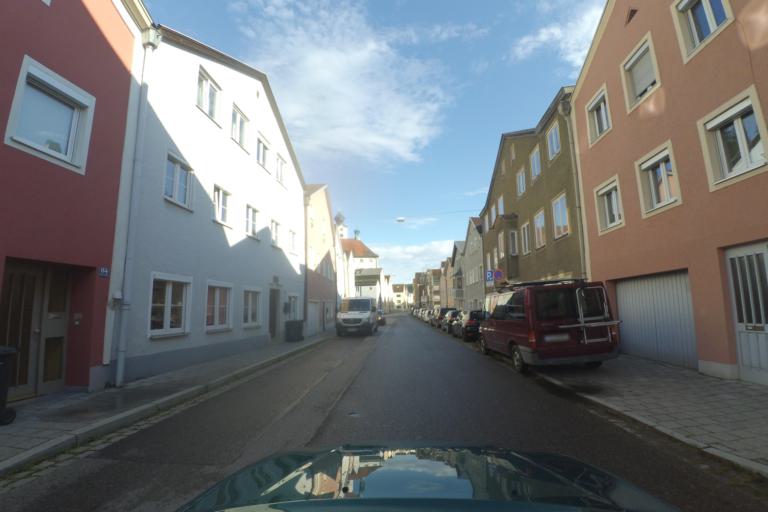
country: DE
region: Bavaria
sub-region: Upper Bavaria
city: Eichstaett
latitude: 48.8970
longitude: 11.1815
